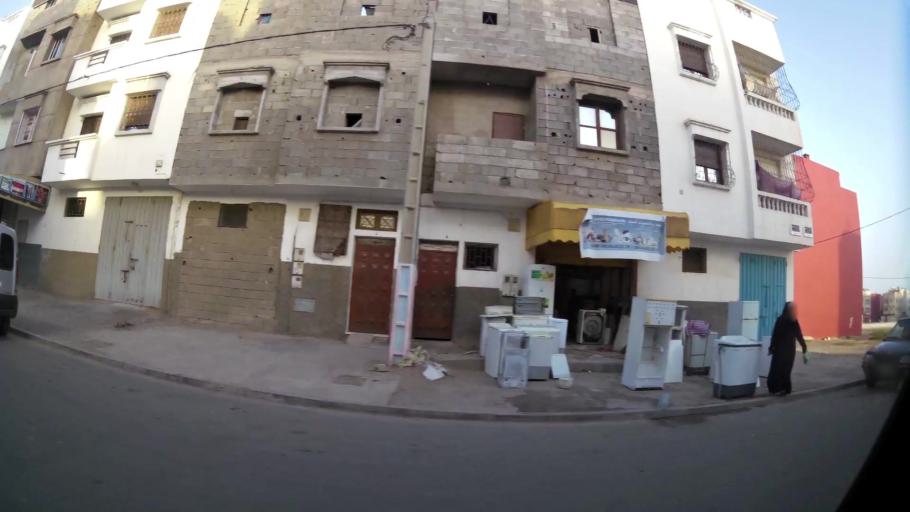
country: MA
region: Oued ed Dahab-Lagouira
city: Dakhla
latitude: 30.3960
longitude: -9.5618
